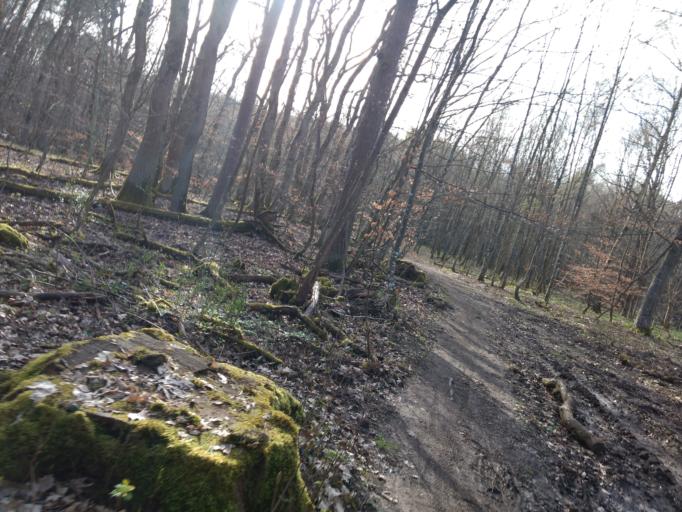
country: DE
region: Saarland
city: Dillingen
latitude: 49.3654
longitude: 6.7360
